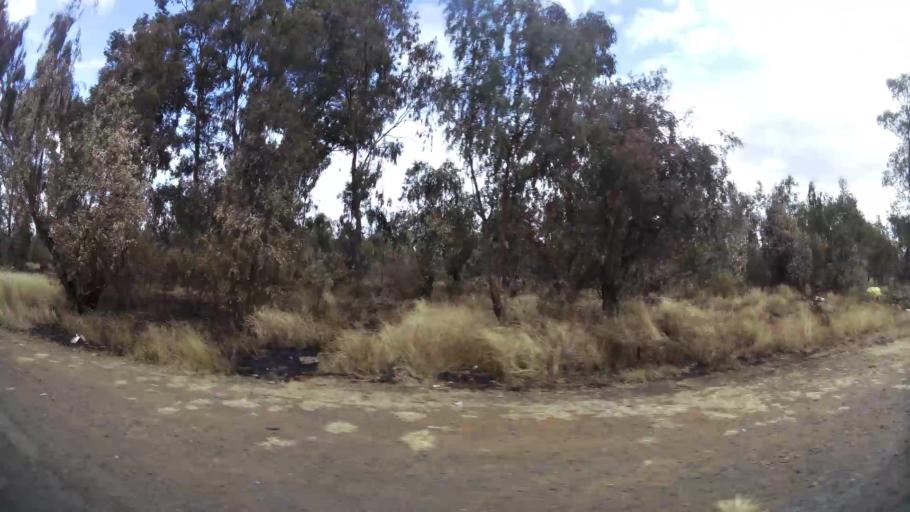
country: ZA
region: Orange Free State
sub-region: Fezile Dabi District Municipality
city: Kroonstad
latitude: -27.6347
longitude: 27.2181
